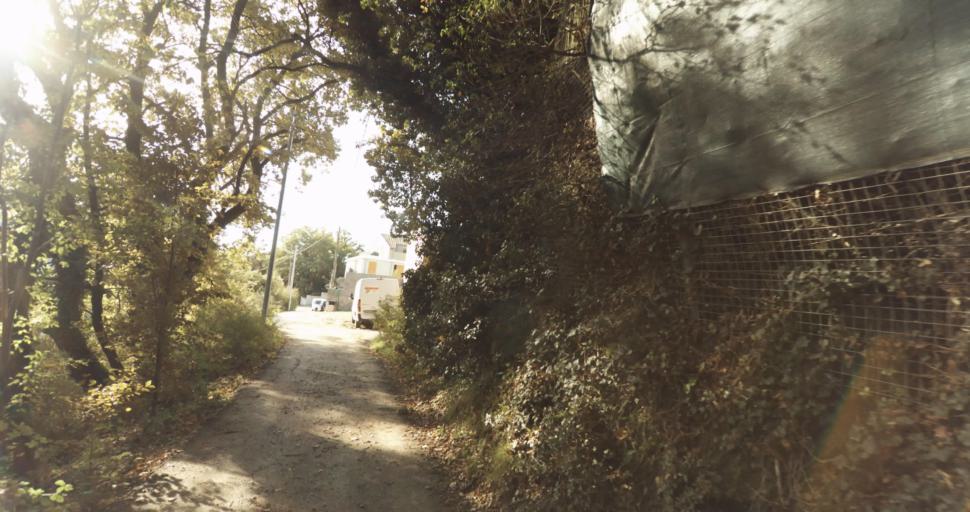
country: FR
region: Provence-Alpes-Cote d'Azur
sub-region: Departement des Bouches-du-Rhone
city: Venelles
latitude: 43.5911
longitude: 5.4751
